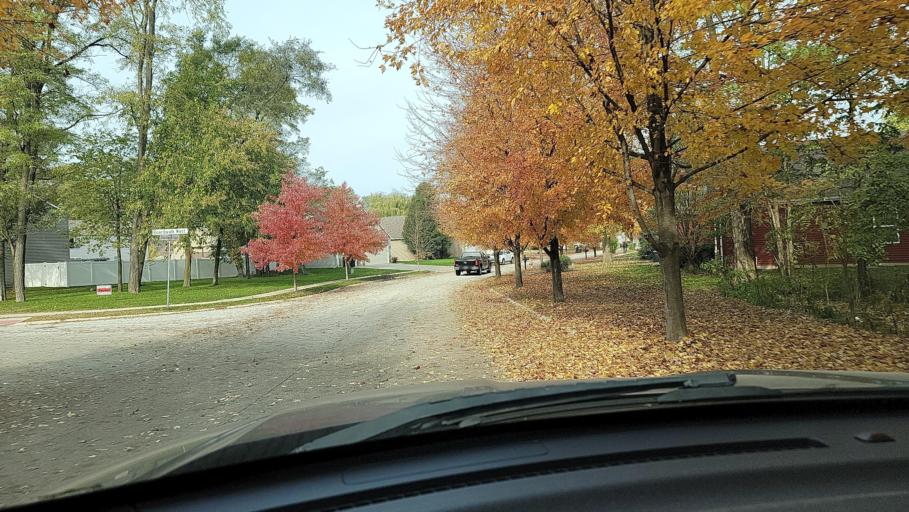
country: US
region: Indiana
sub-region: Porter County
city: Portage
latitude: 41.5947
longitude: -87.1692
